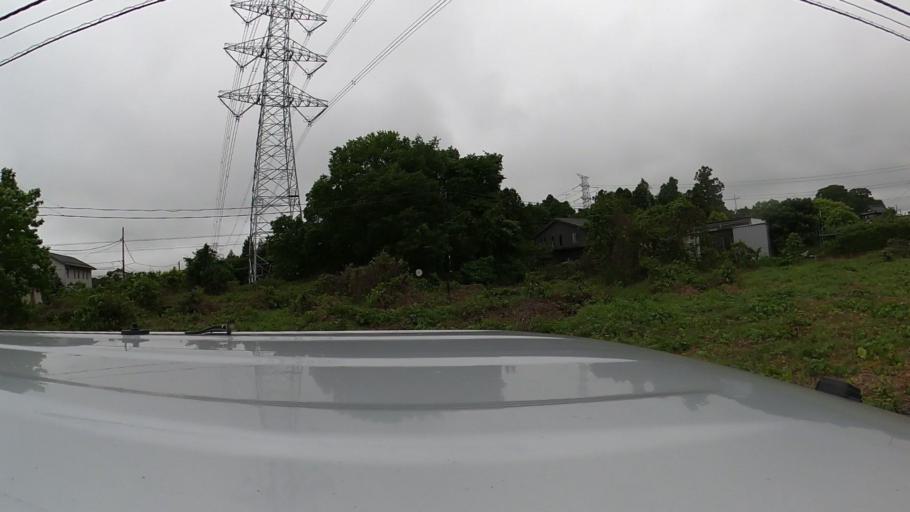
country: JP
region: Ibaraki
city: Ushiku
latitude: 36.0022
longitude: 140.1290
